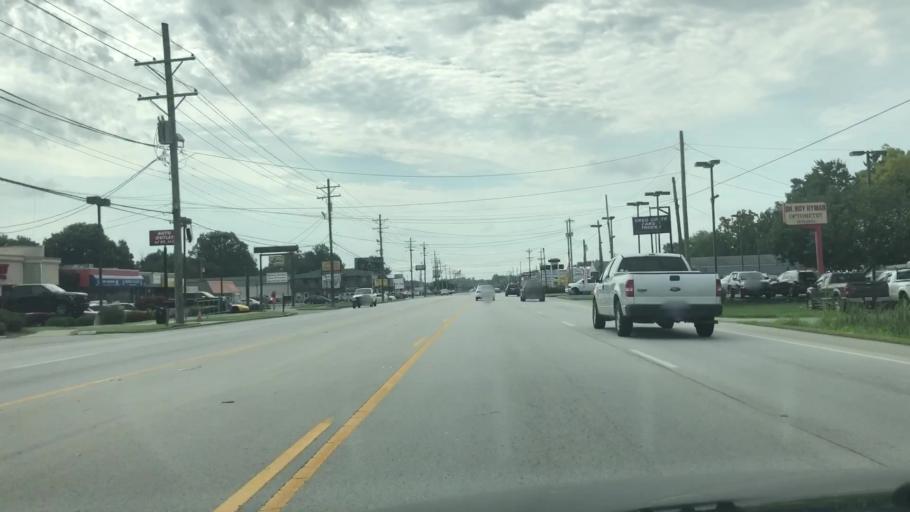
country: US
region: Kentucky
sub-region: Jefferson County
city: Audubon Park
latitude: 38.1732
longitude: -85.7113
